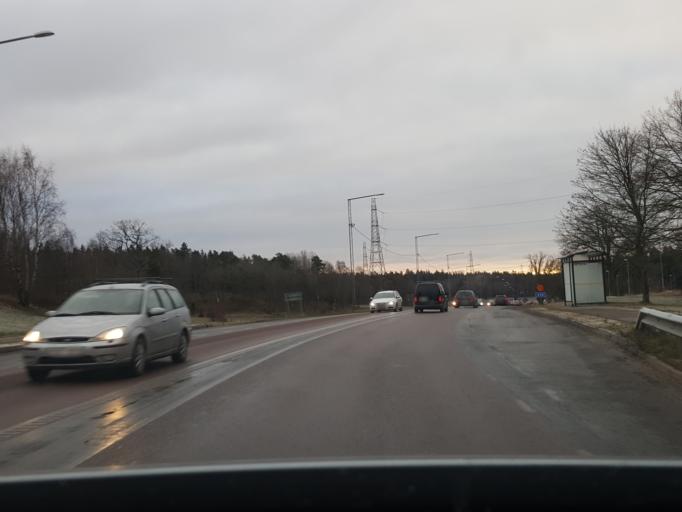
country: SE
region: Stockholm
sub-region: Botkyrka Kommun
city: Alby
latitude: 59.2327
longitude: 17.8430
